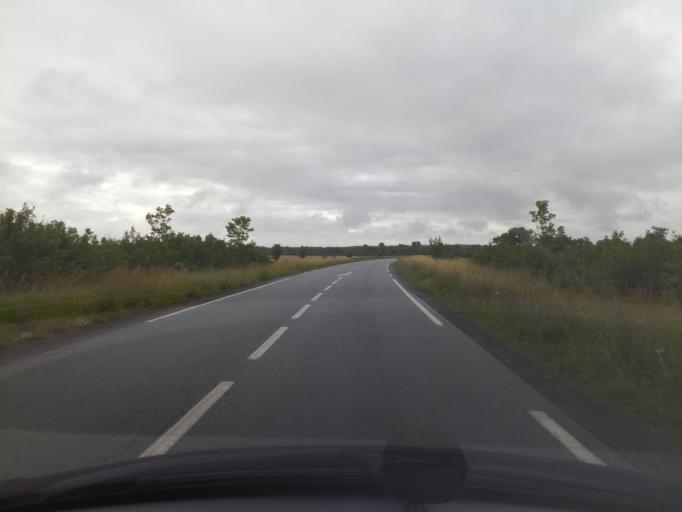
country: FR
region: Poitou-Charentes
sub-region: Departement de la Charente-Maritime
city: Courcon
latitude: 46.1949
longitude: -0.8664
